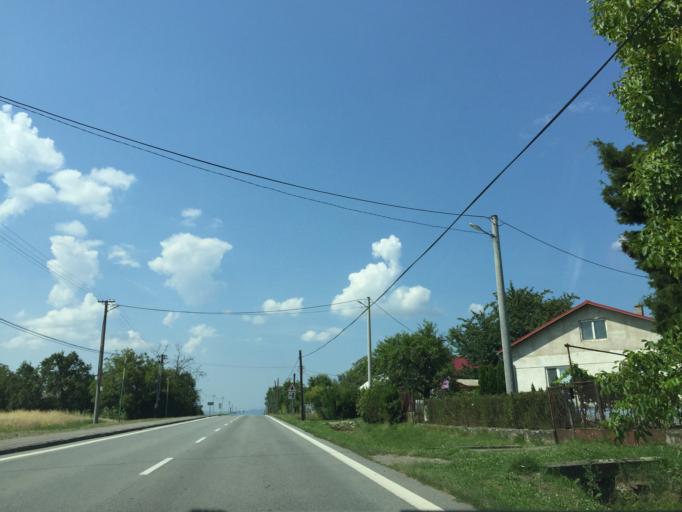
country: UA
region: Zakarpattia
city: Storozhnytsya
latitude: 48.6842
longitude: 22.2431
